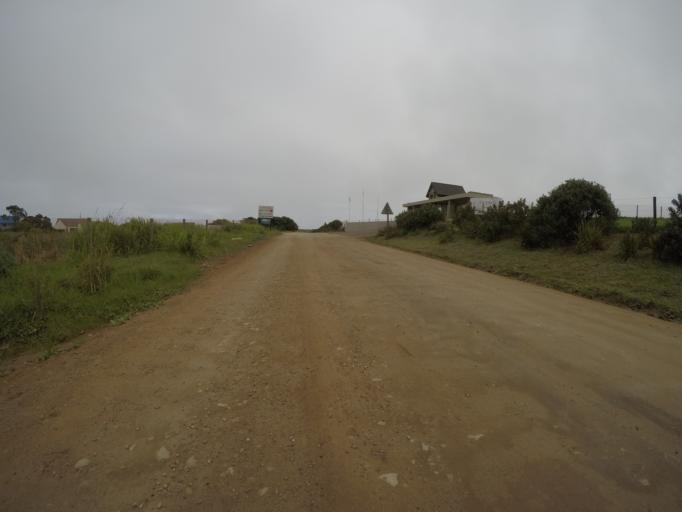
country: ZA
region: Eastern Cape
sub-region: Cacadu District Municipality
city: Kareedouw
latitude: -34.0706
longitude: 24.2348
